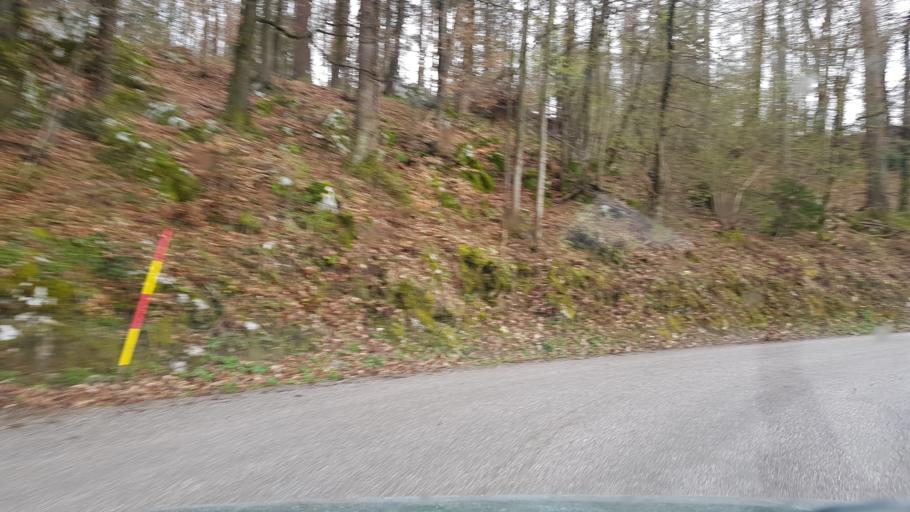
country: SI
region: Tolmin
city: Tolmin
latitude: 46.1110
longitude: 13.8417
